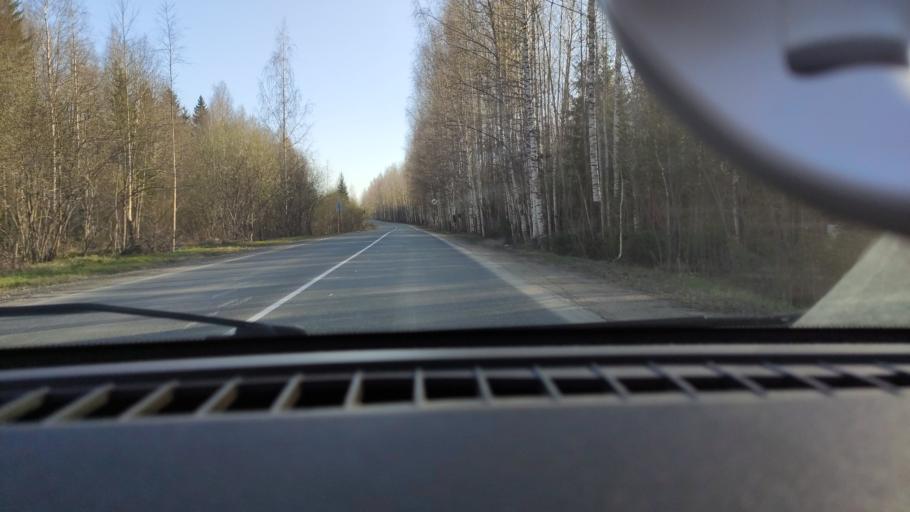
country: RU
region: Perm
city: Polazna
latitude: 58.1227
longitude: 56.4334
